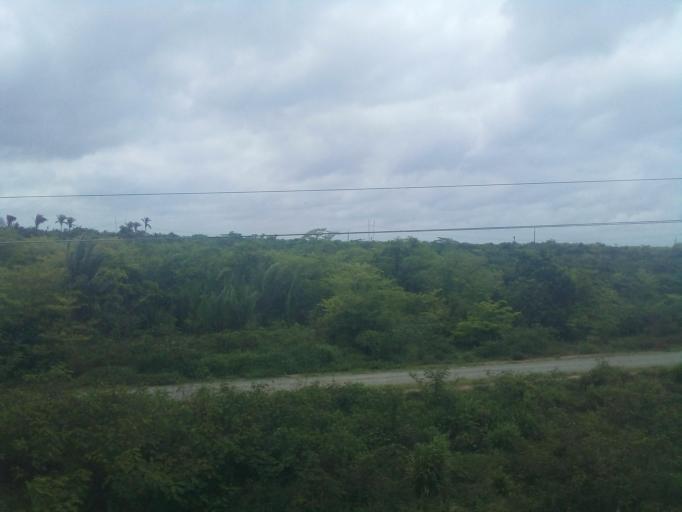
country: BR
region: Maranhao
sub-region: Arari
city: Arari
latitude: -3.5755
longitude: -44.7424
